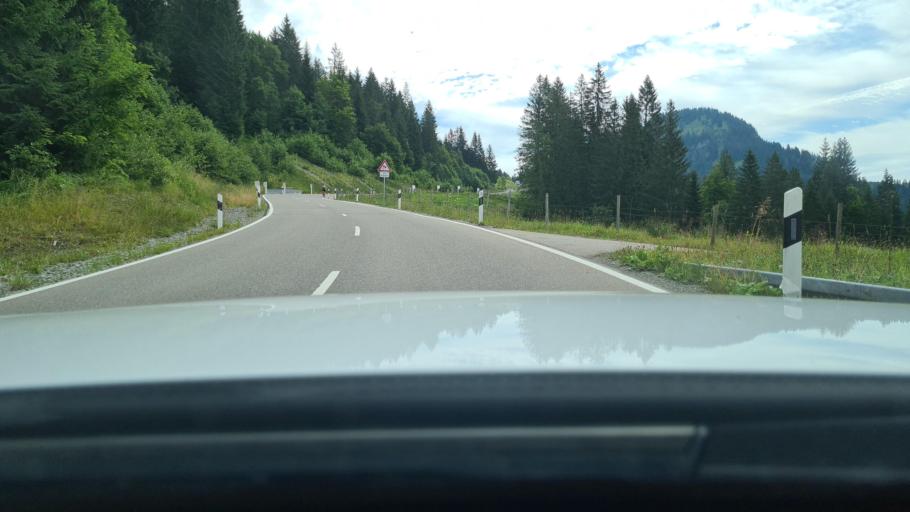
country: DE
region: Bavaria
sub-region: Swabia
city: Balderschwang
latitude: 47.4356
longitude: 10.1500
